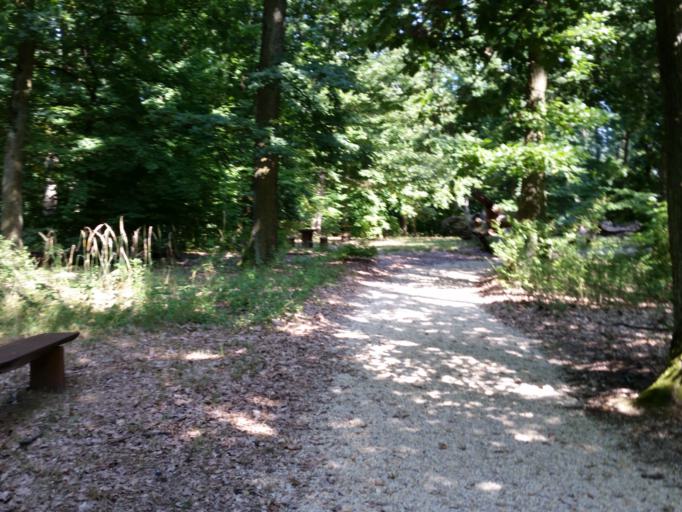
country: HU
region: Vas
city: Sarvar
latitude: 47.1853
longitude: 16.9949
